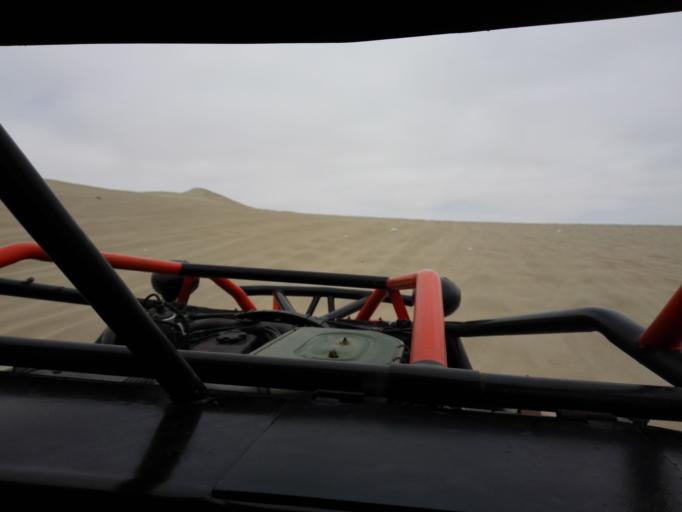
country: PE
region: Ica
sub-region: Provincia de Ica
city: Ica
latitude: -14.0869
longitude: -75.7721
